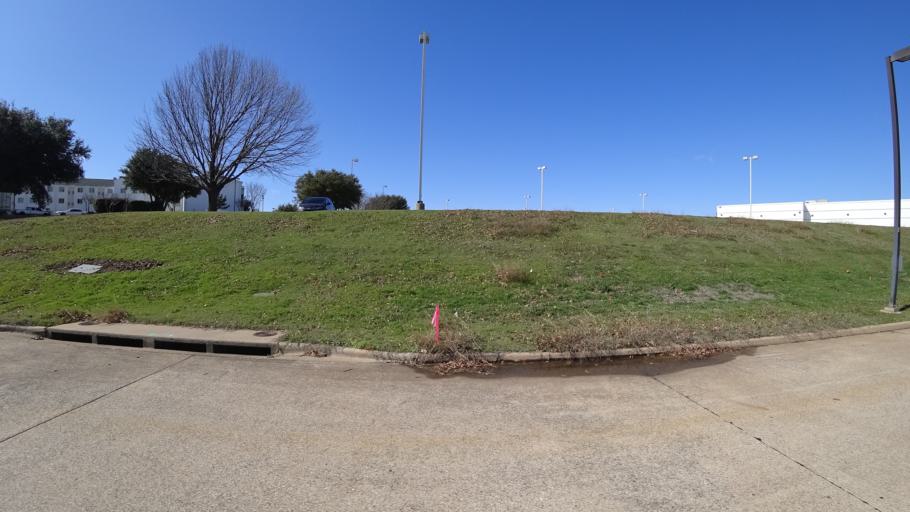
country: US
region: Texas
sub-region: Denton County
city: Lewisville
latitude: 33.0221
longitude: -96.9826
